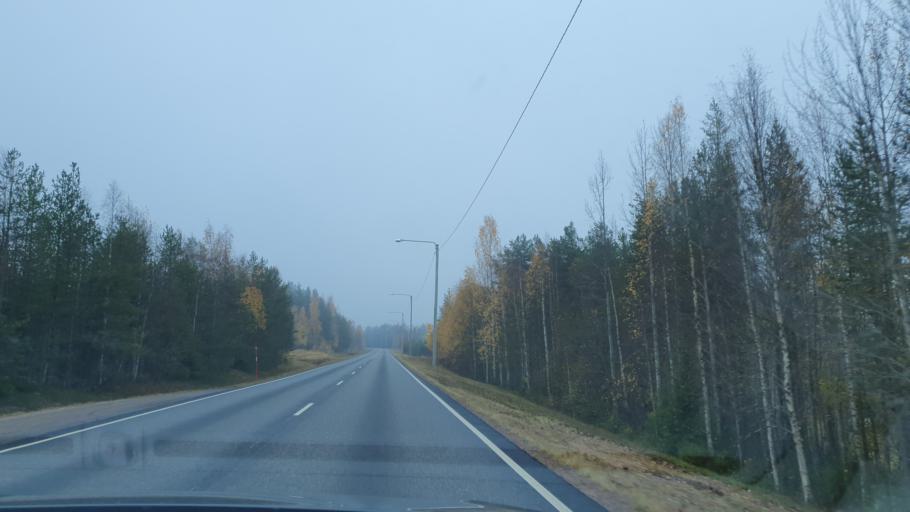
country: FI
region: Lapland
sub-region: Tunturi-Lappi
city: Kittilae
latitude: 67.0347
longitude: 25.1051
